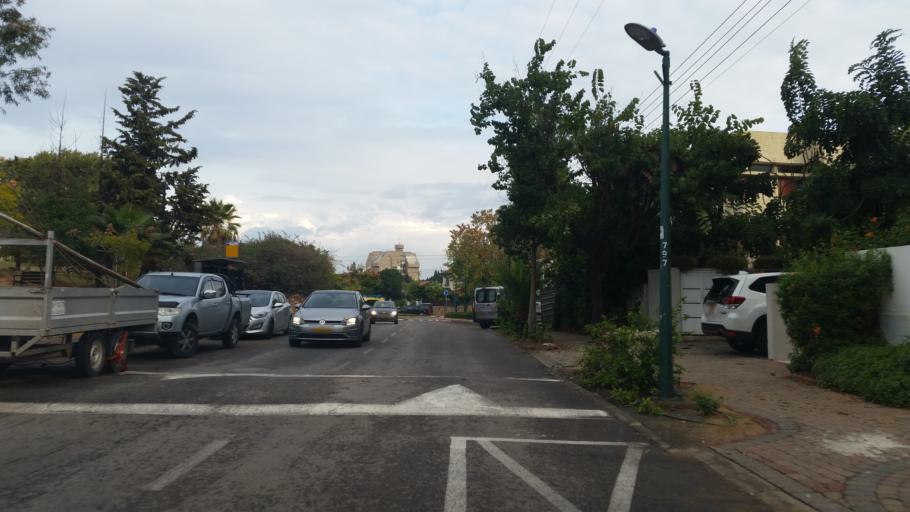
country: IL
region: Tel Aviv
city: Ramat HaSharon
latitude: 32.1557
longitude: 34.8475
